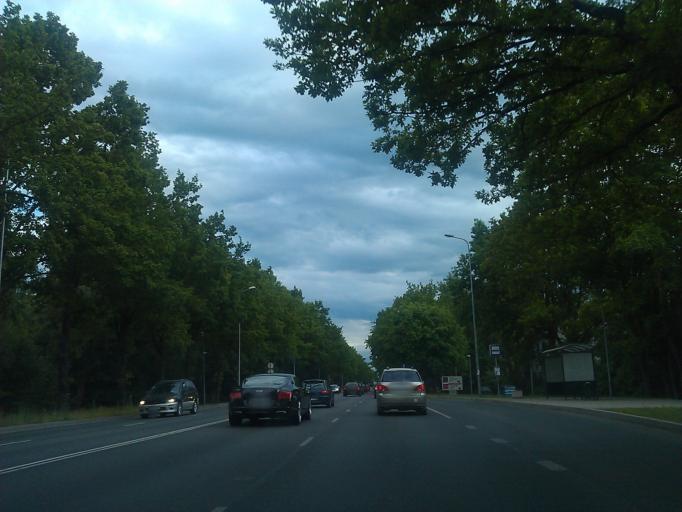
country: LV
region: Marupe
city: Marupe
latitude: 56.9050
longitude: 24.0823
